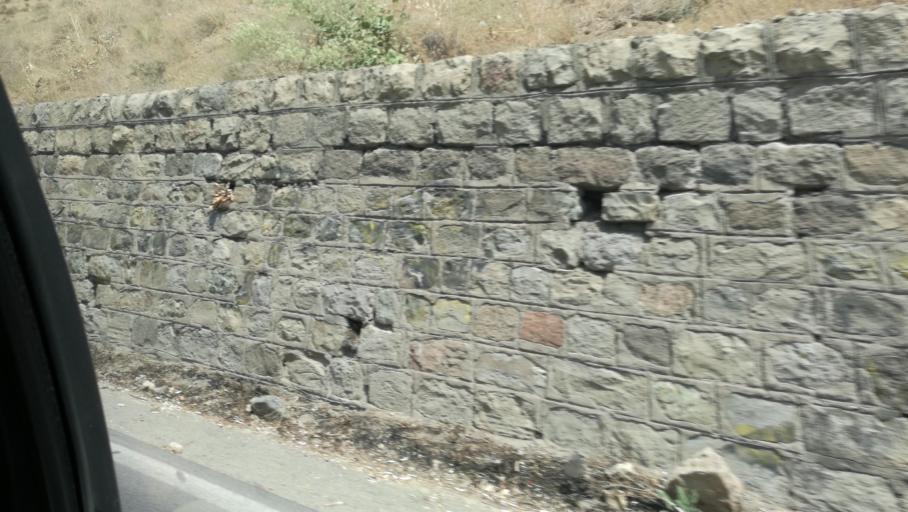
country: IR
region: Alborz
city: Karaj
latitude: 35.9257
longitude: 51.0589
